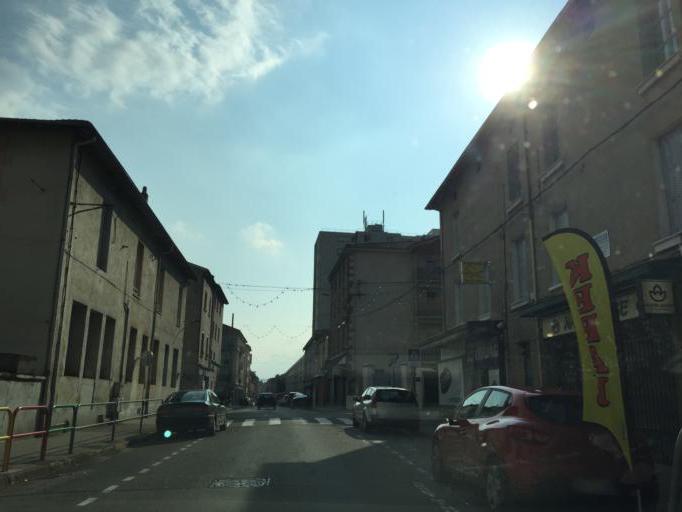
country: FR
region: Rhone-Alpes
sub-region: Departement de la Loire
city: Rive-de-Gier
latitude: 45.5318
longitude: 4.6231
